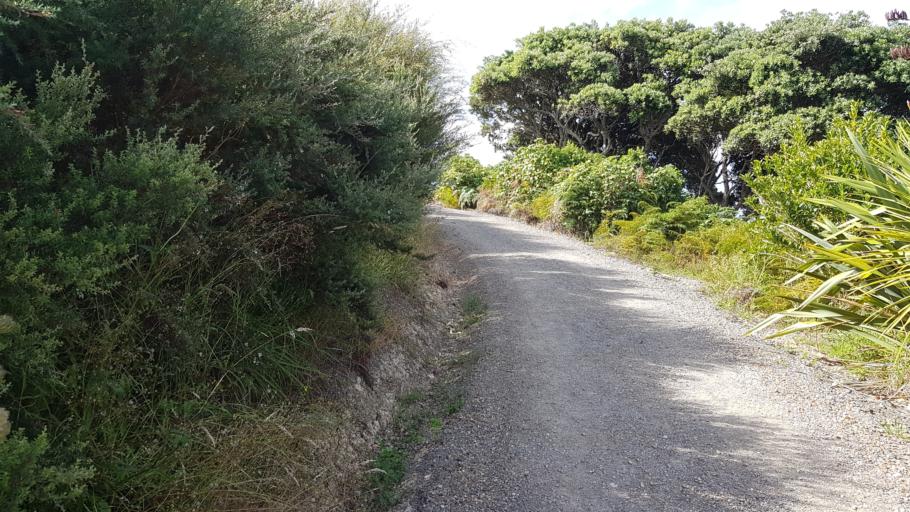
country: NZ
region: Auckland
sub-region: Auckland
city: Rothesay Bay
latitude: -36.6740
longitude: 174.7469
